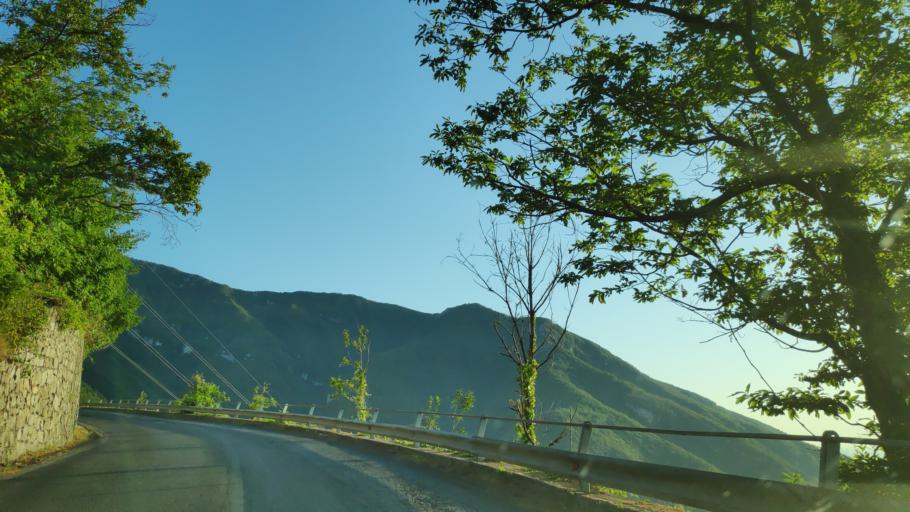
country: IT
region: Campania
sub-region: Provincia di Salerno
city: Corbara
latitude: 40.7194
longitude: 14.6031
